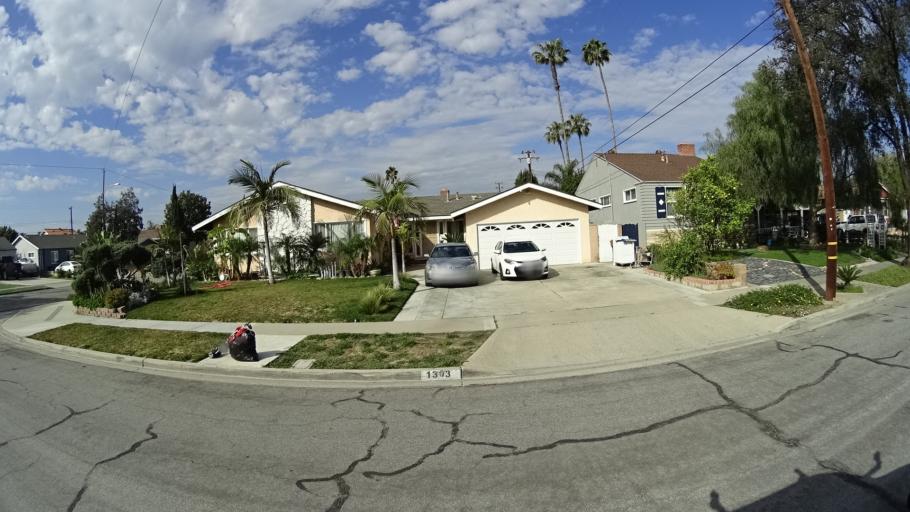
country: US
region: California
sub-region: Orange County
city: Placentia
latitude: 33.8522
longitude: -117.8842
